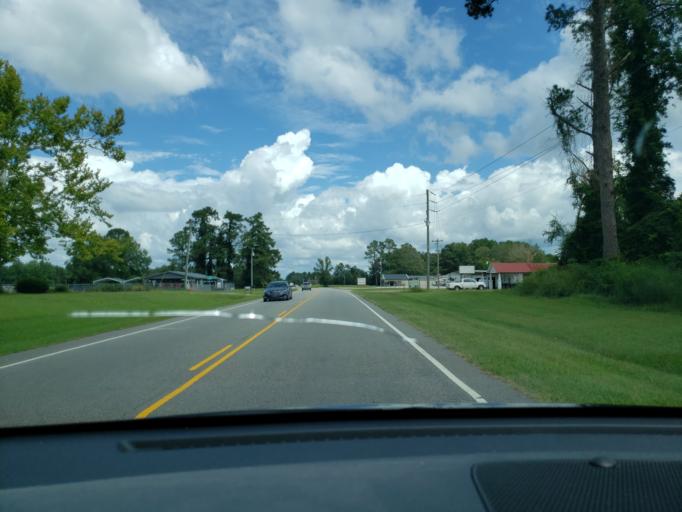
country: US
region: North Carolina
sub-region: Columbus County
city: Brunswick
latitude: 34.2146
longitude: -78.7573
